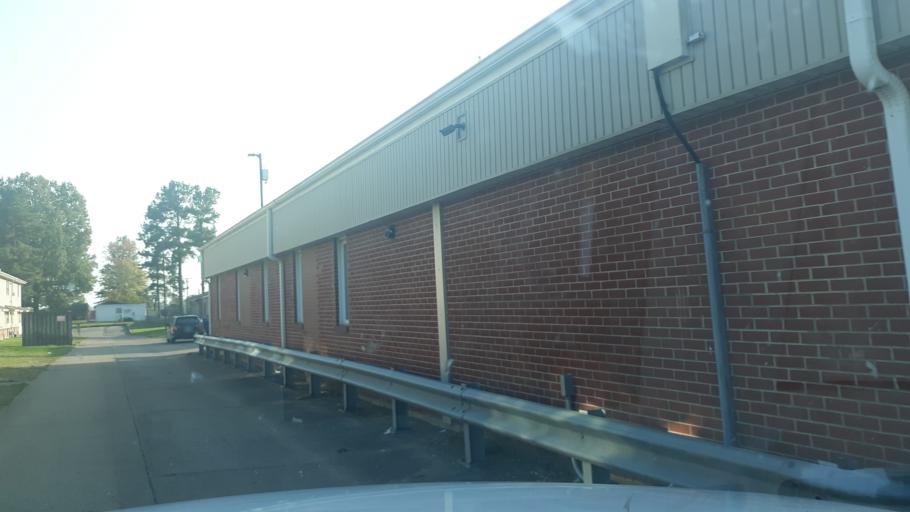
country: US
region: Illinois
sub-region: Saline County
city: Harrisburg
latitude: 37.7203
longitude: -88.5526
